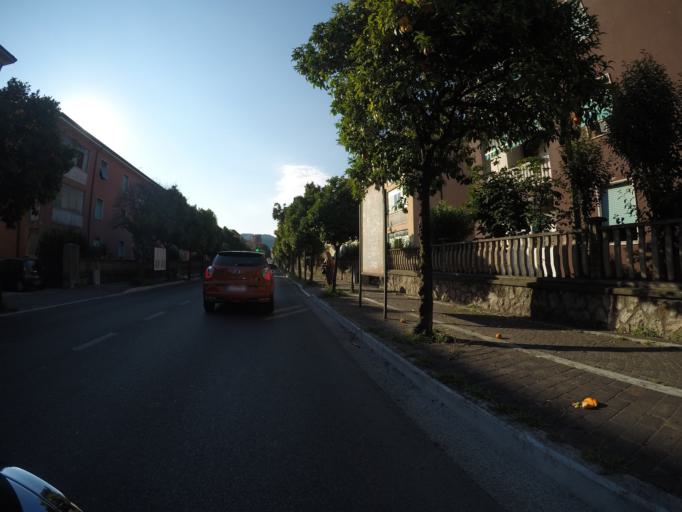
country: IT
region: Tuscany
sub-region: Provincia di Massa-Carrara
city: Massa
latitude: 44.0325
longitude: 10.1429
